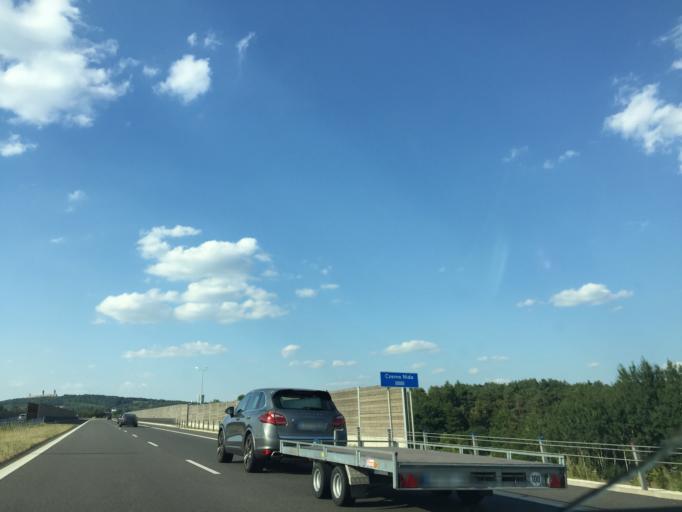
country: PL
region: Swietokrzyskie
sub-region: Powiat kielecki
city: Checiny
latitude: 50.7715
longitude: 20.4640
